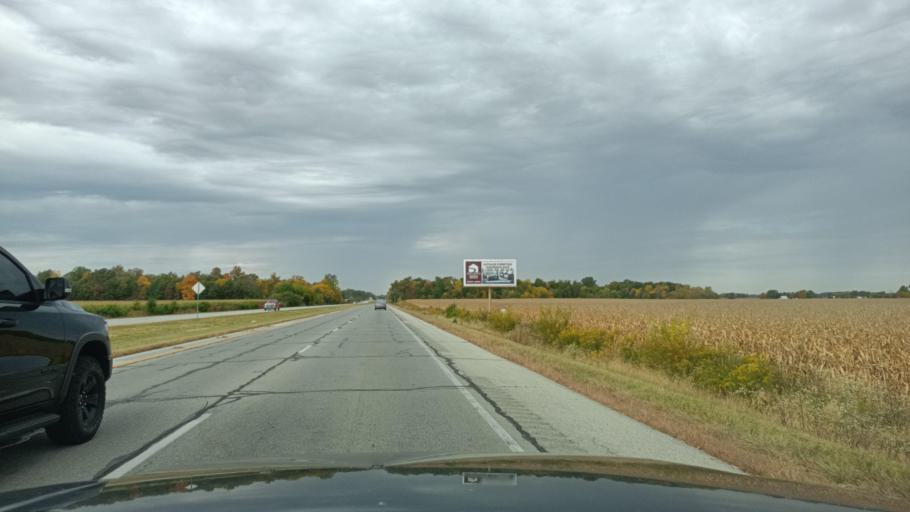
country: US
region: Indiana
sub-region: Delaware County
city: Yorktown
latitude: 40.2194
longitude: -85.4838
